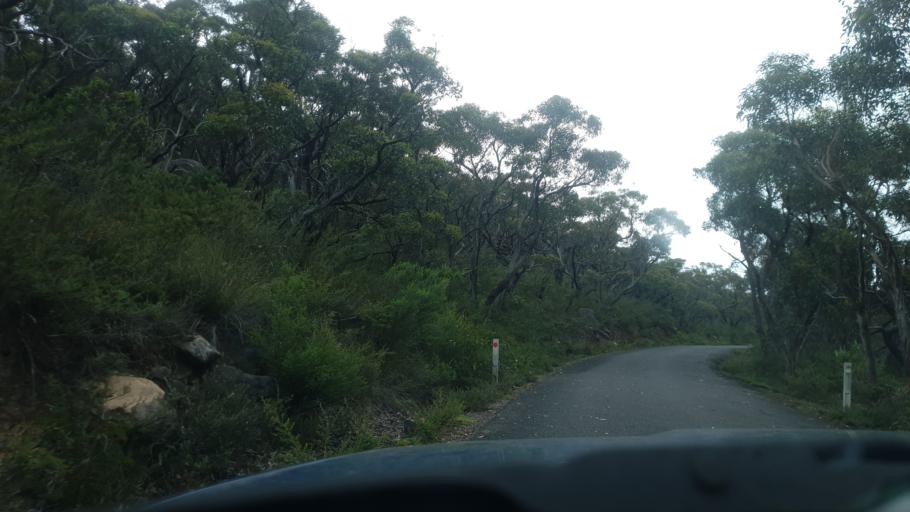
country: AU
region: Victoria
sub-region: Northern Grampians
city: Stawell
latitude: -37.2824
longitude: 142.5872
